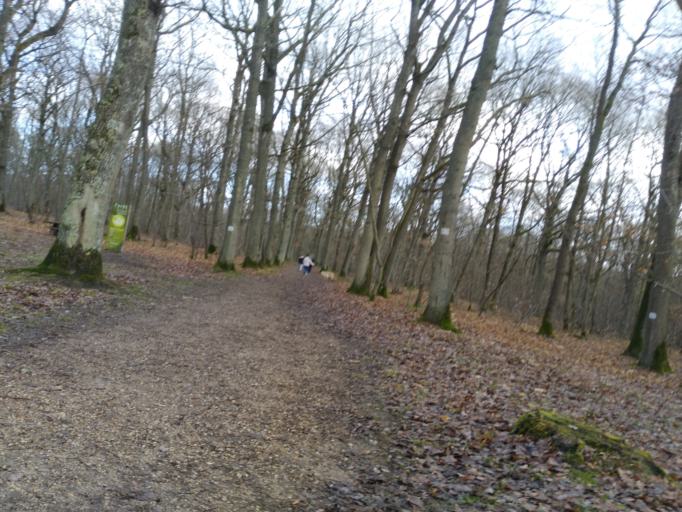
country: FR
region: Ile-de-France
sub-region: Departement des Yvelines
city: Neauphle-le-Chateau
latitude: 48.8062
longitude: 1.9319
